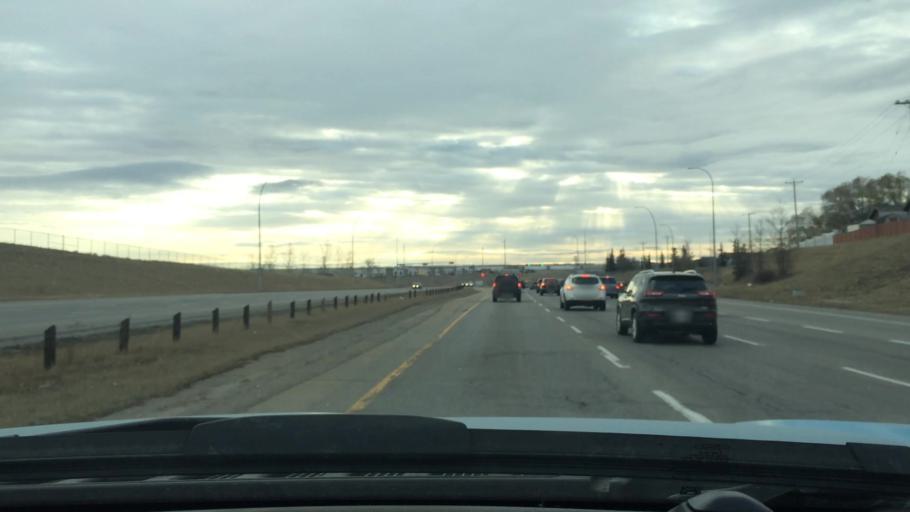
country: CA
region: Alberta
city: Calgary
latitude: 51.1292
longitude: -114.0558
